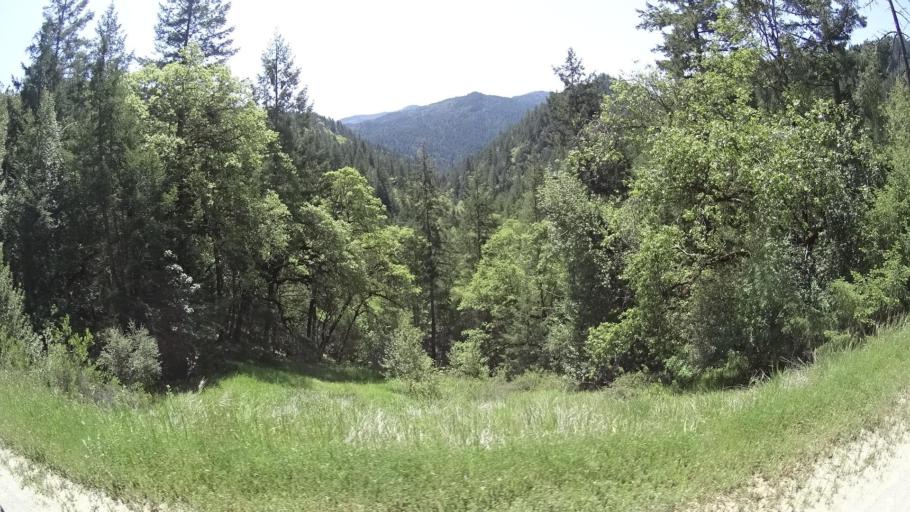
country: US
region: California
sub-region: Humboldt County
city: Redway
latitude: 40.2026
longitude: -123.5219
